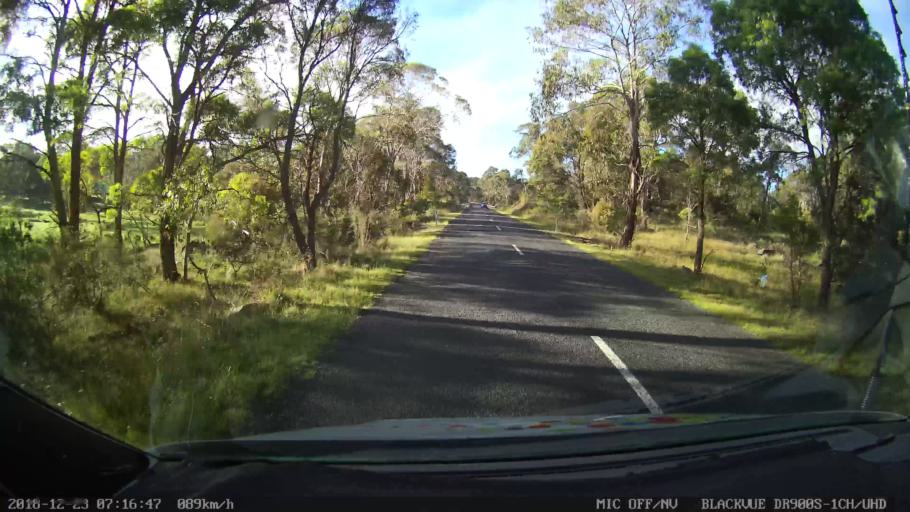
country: AU
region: New South Wales
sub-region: Bellingen
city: Dorrigo
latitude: -30.4602
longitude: 152.3080
